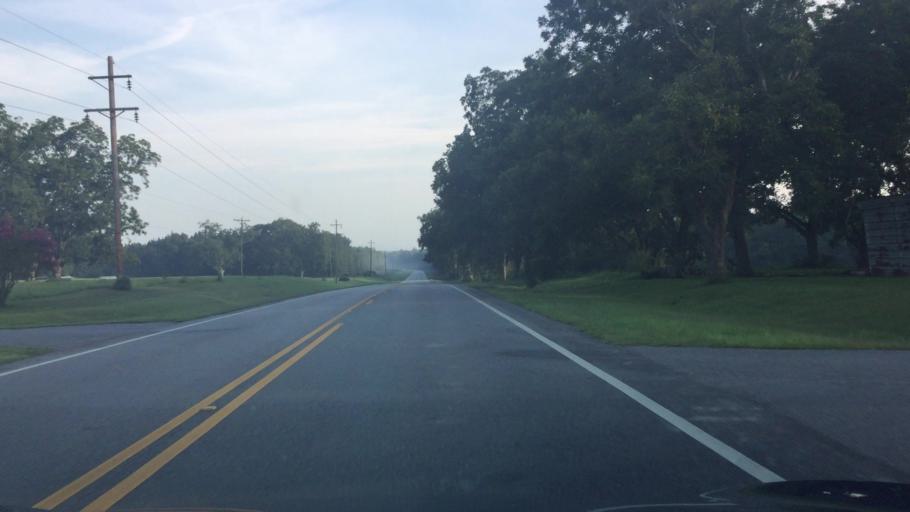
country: US
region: Alabama
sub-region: Covington County
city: Florala
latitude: 31.0500
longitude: -86.3875
